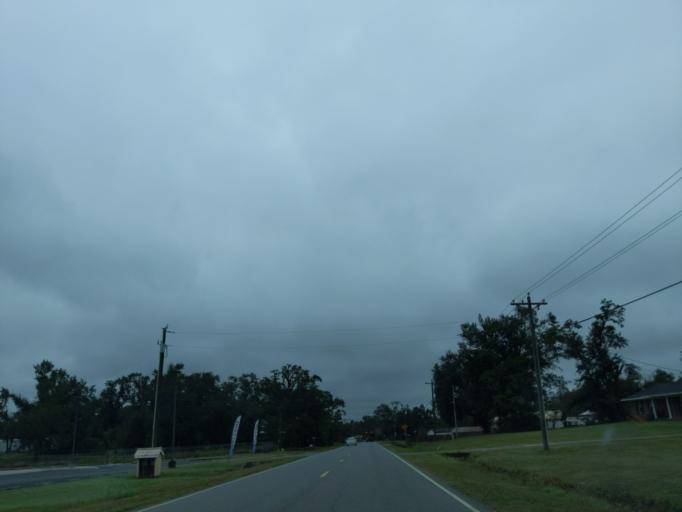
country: US
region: Florida
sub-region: Jackson County
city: Sneads
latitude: 30.7126
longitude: -84.9325
